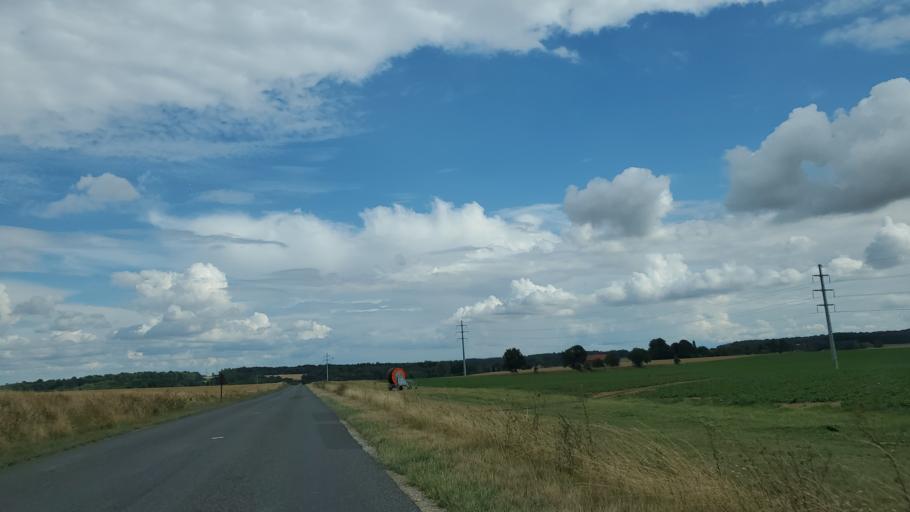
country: FR
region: Ile-de-France
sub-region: Departement de Seine-et-Marne
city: Chailly-en-Brie
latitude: 48.7836
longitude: 3.1526
